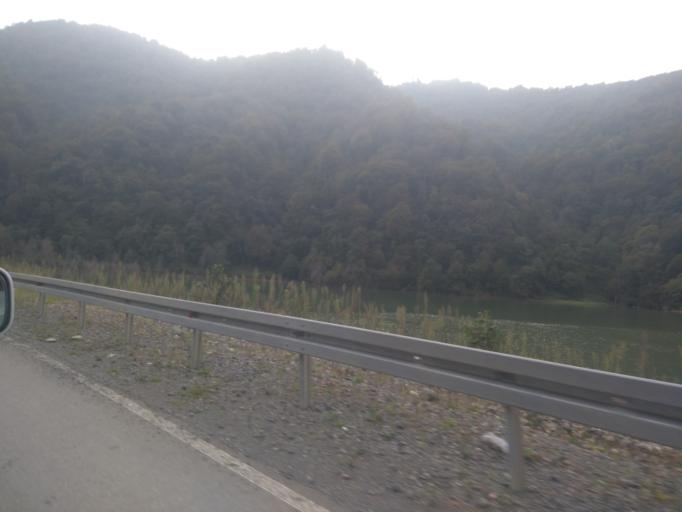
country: GE
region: Ajaria
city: Khelvachauri
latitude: 41.5457
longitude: 41.7063
